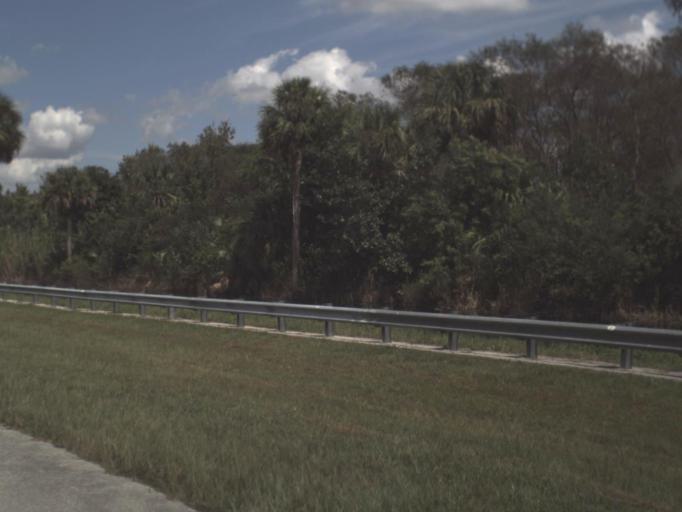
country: US
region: Florida
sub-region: Collier County
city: Orangetree
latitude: 26.1227
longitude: -81.3448
